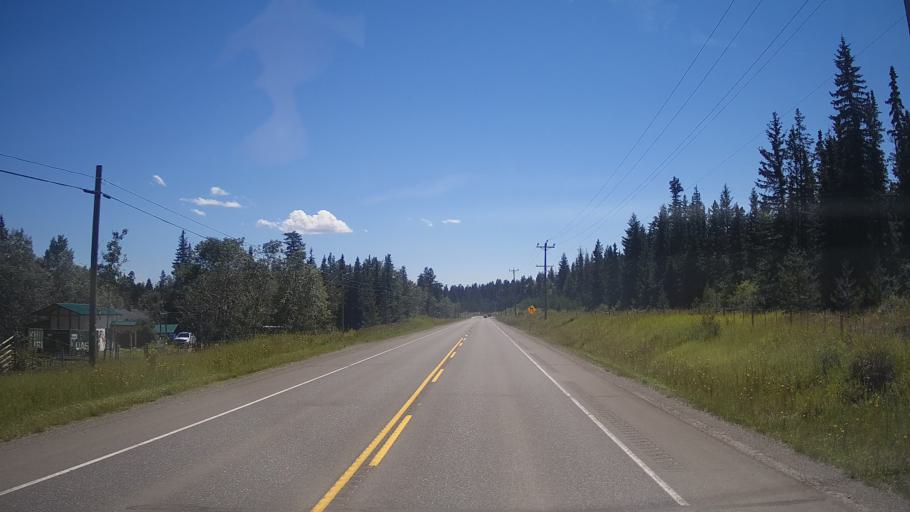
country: CA
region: British Columbia
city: Cache Creek
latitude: 51.1901
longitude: -121.5261
